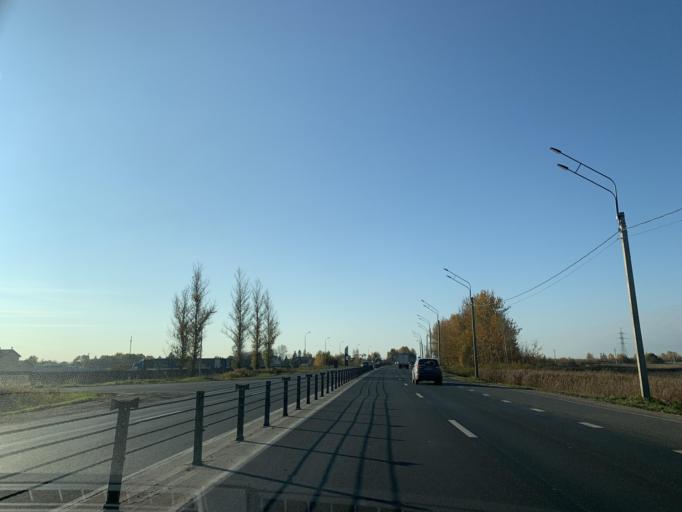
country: RU
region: Jaroslavl
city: Yaroslavl
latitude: 57.6406
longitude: 39.7476
